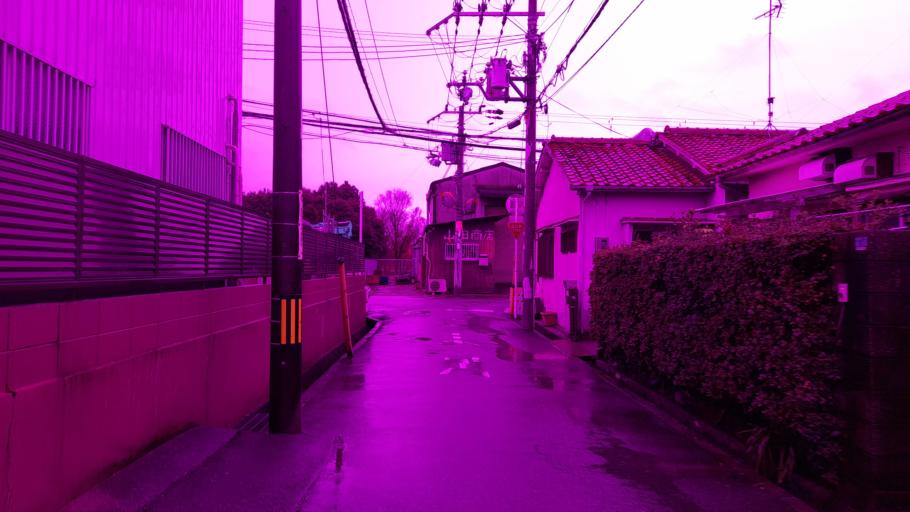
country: JP
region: Osaka
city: Toyonaka
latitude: 34.7714
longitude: 135.4556
